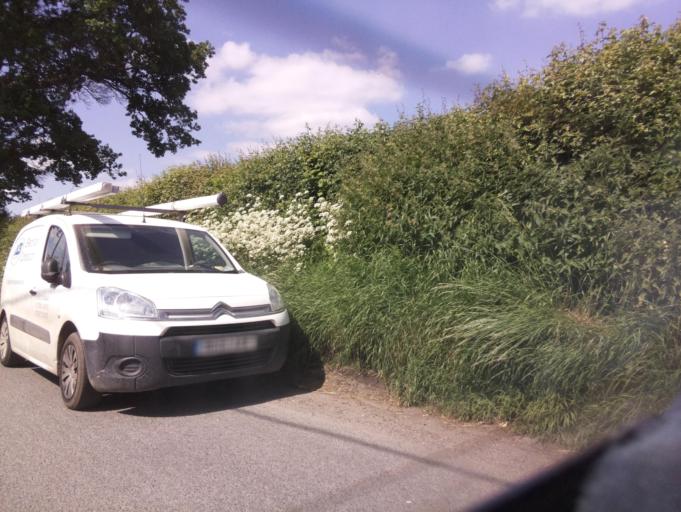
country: GB
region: England
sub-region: Wiltshire
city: Huish
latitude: 51.3522
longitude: -1.8014
